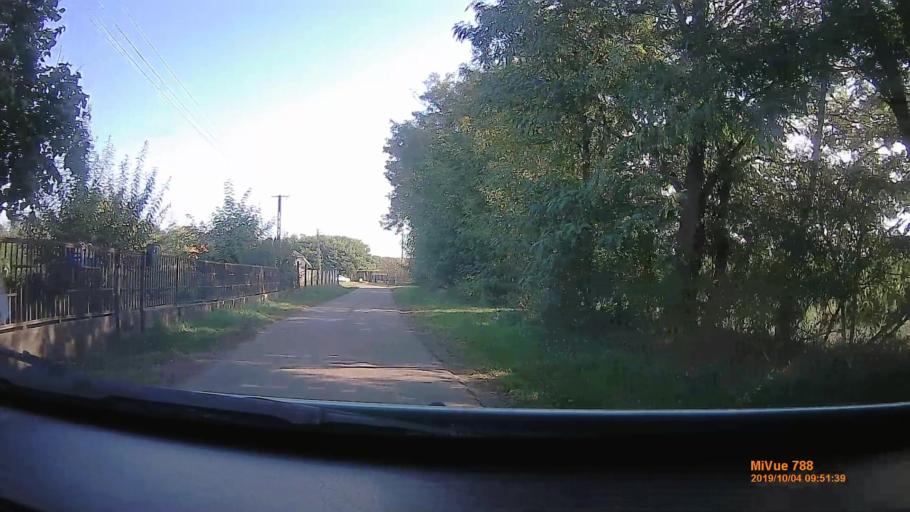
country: HU
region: Szabolcs-Szatmar-Bereg
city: Nyiregyhaza
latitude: 47.9447
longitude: 21.6596
